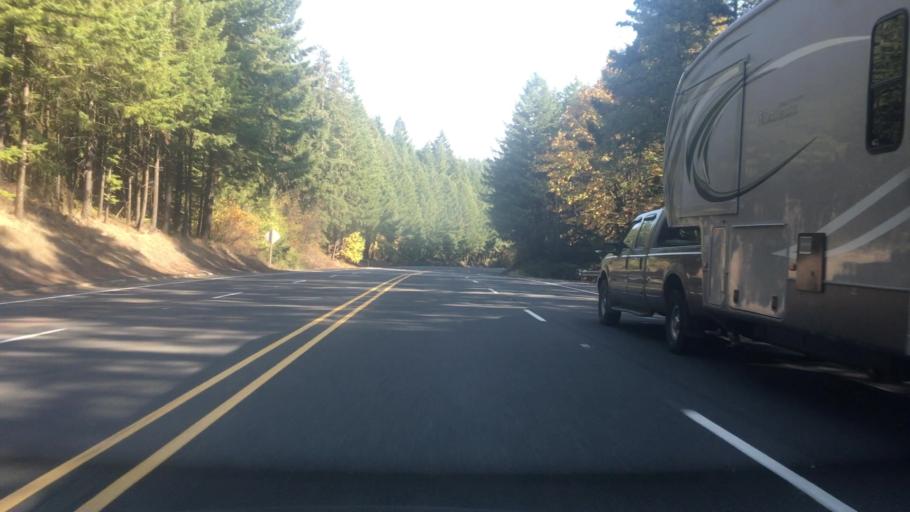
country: US
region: Oregon
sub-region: Polk County
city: Grand Ronde
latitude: 45.0609
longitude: -123.6945
